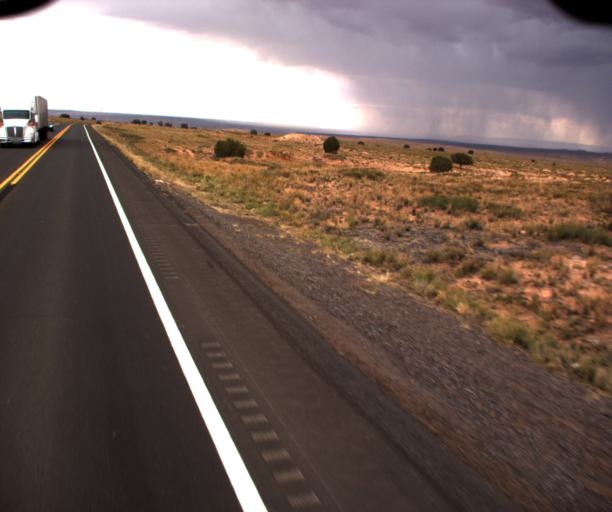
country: US
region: Arizona
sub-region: Coconino County
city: Tuba City
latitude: 36.2403
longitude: -111.0252
